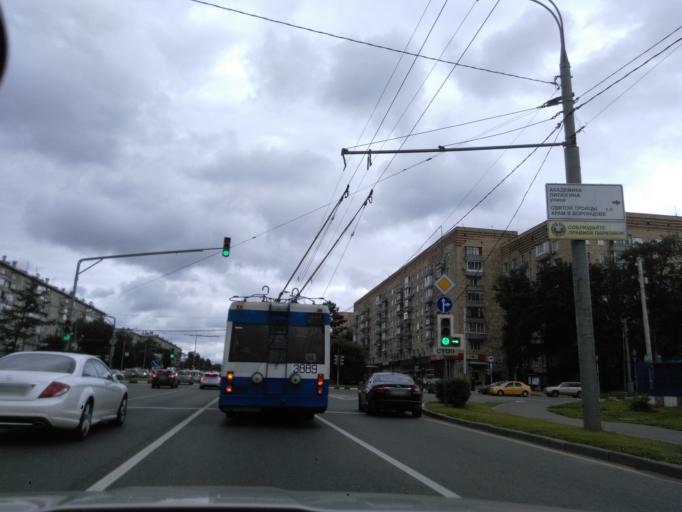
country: RU
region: Moskovskaya
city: Semenovskoye
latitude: 55.6732
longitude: 37.5237
